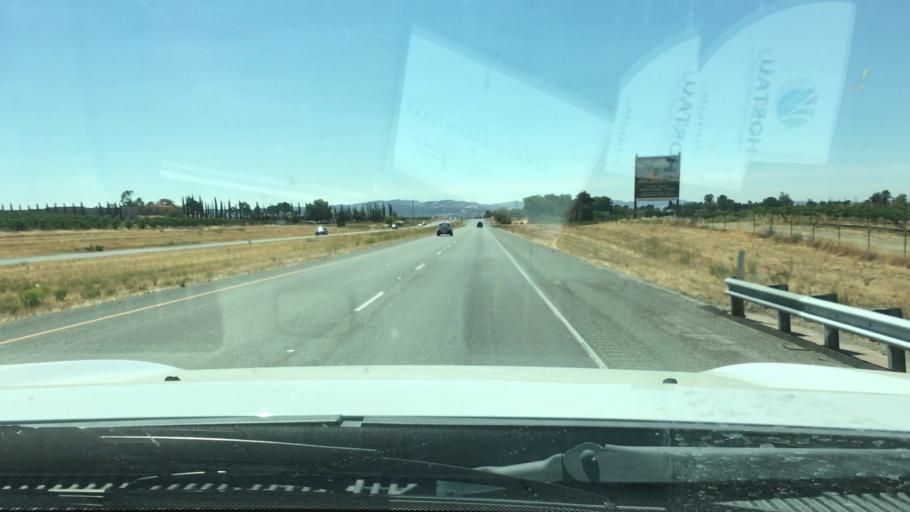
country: US
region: California
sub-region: San Luis Obispo County
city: Paso Robles
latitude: 35.6601
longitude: -120.5892
